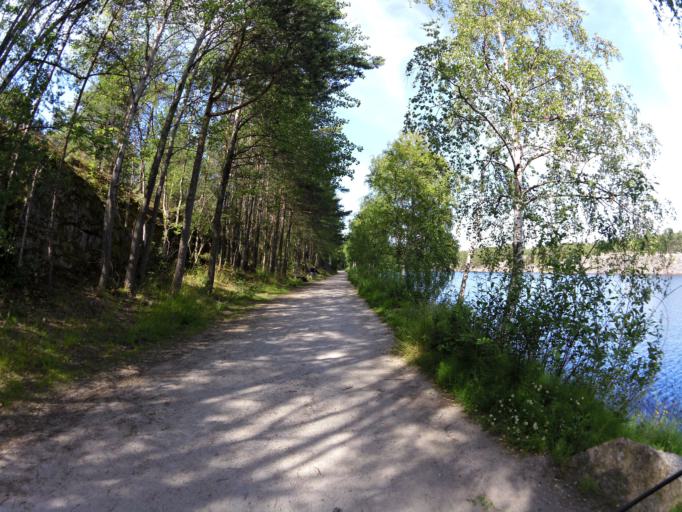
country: NO
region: Ostfold
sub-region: Fredrikstad
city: Fredrikstad
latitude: 59.2334
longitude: 10.9474
